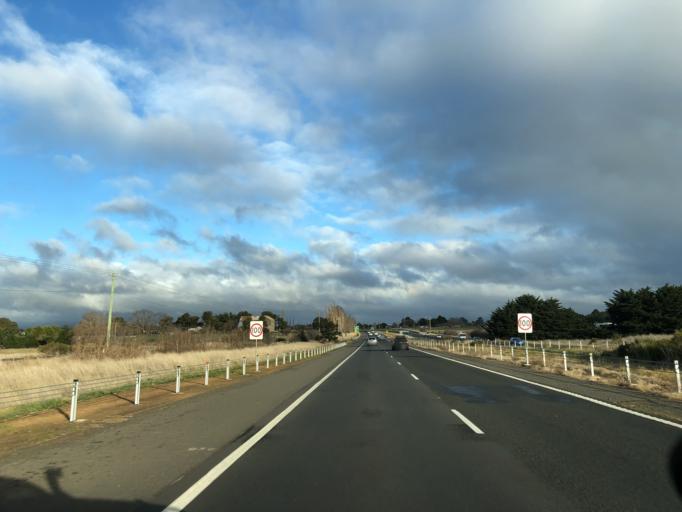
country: AU
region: Victoria
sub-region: Mount Alexander
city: Castlemaine
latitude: -37.2134
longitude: 144.4139
